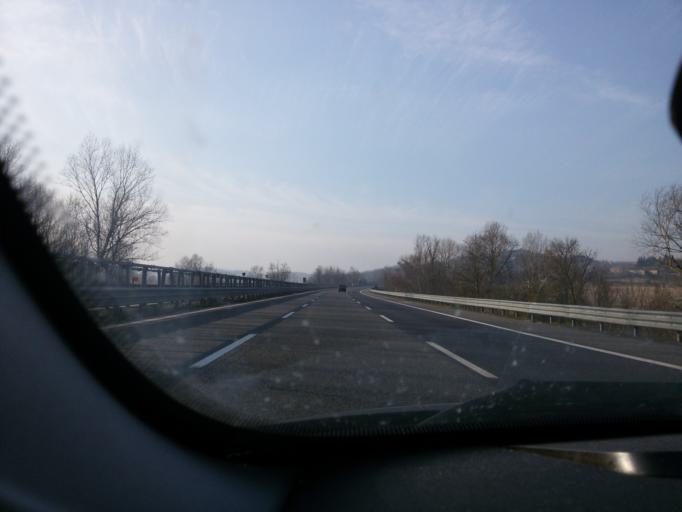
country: IT
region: Piedmont
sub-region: Provincia di Alessandria
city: Castelletto Monferrato
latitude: 44.9807
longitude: 8.5420
